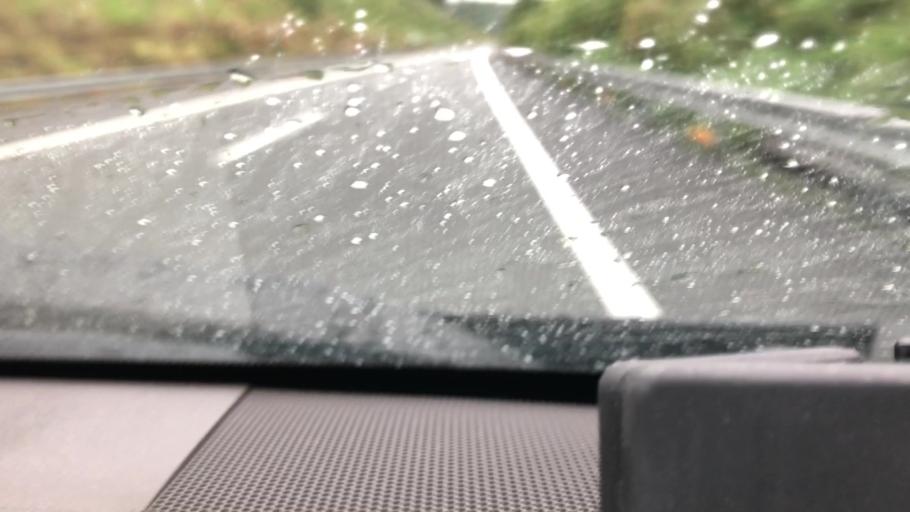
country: JP
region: Shizuoka
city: Mishima
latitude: 35.2070
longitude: 138.8865
